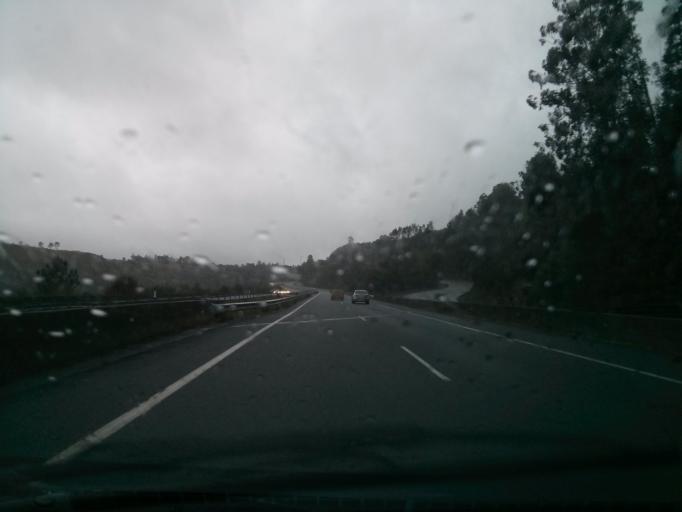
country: ES
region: Galicia
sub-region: Provincia de Ourense
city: Melon
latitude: 42.2456
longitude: -8.2267
